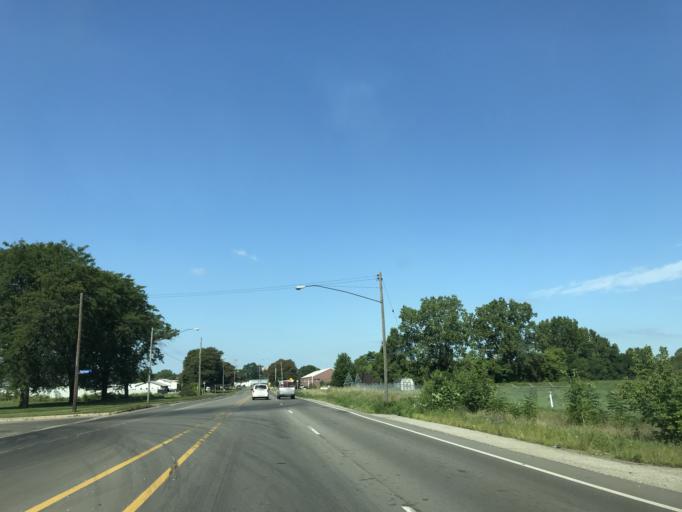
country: US
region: Michigan
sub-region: Kalamazoo County
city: Eastwood
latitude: 42.2851
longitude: -85.5555
